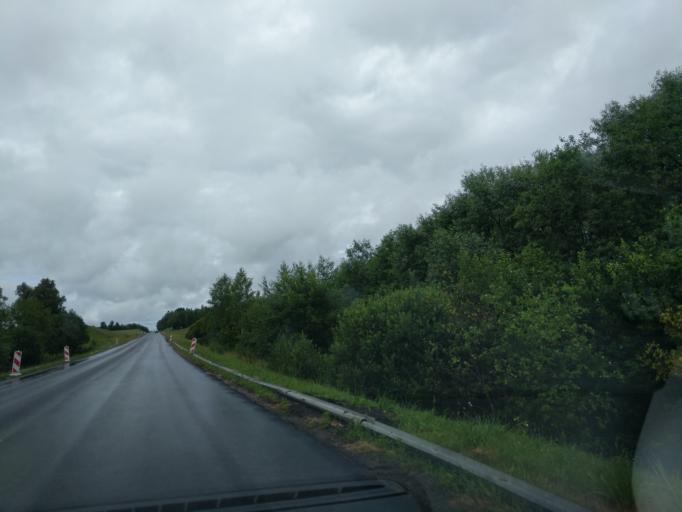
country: BY
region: Minsk
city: Il'ya
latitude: 54.3061
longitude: 27.4741
